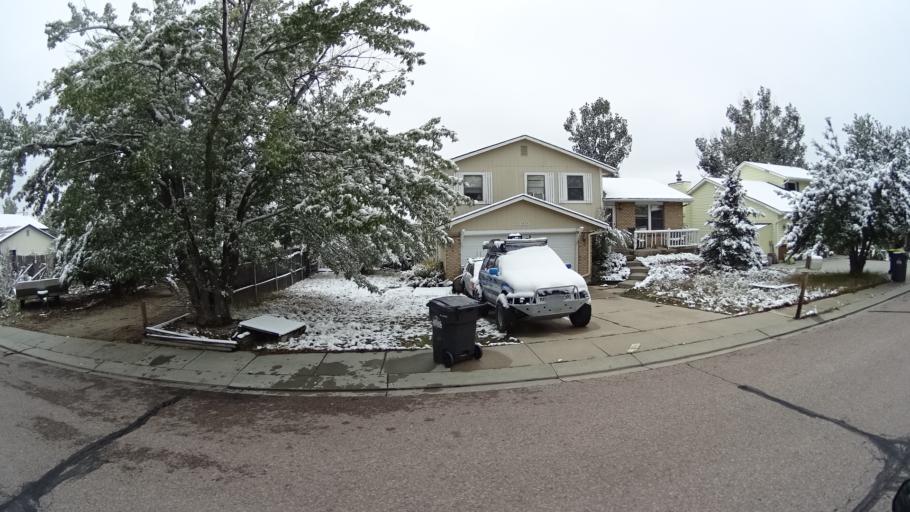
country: US
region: Colorado
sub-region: El Paso County
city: Colorado Springs
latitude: 38.9226
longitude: -104.7861
